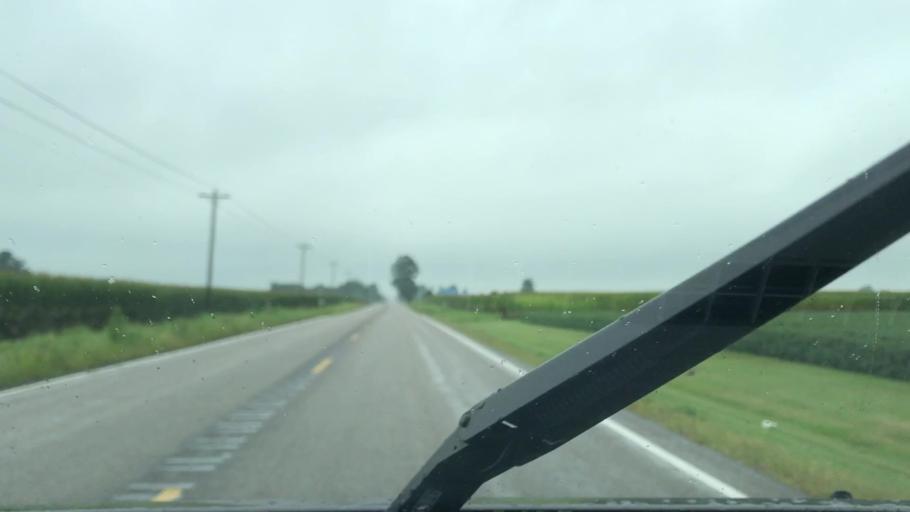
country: US
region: Indiana
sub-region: Boone County
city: Dale
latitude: 40.1268
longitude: -86.3863
